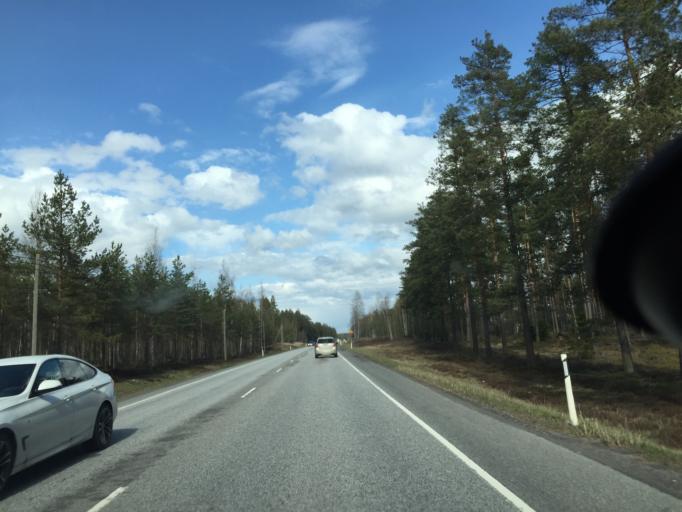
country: FI
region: Uusimaa
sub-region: Raaseporin
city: Pohja
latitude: 60.0240
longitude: 23.5787
